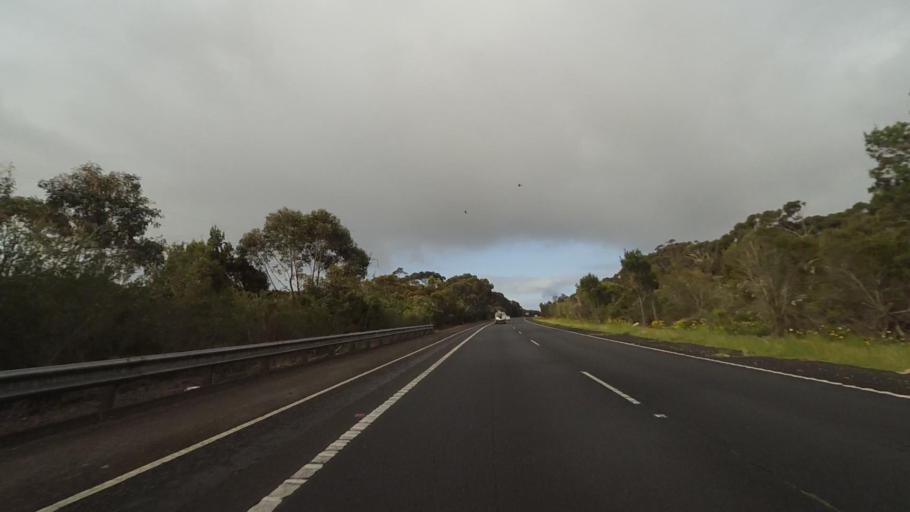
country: AU
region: New South Wales
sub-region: Wollongong
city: Bulli
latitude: -34.2491
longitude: 150.9356
